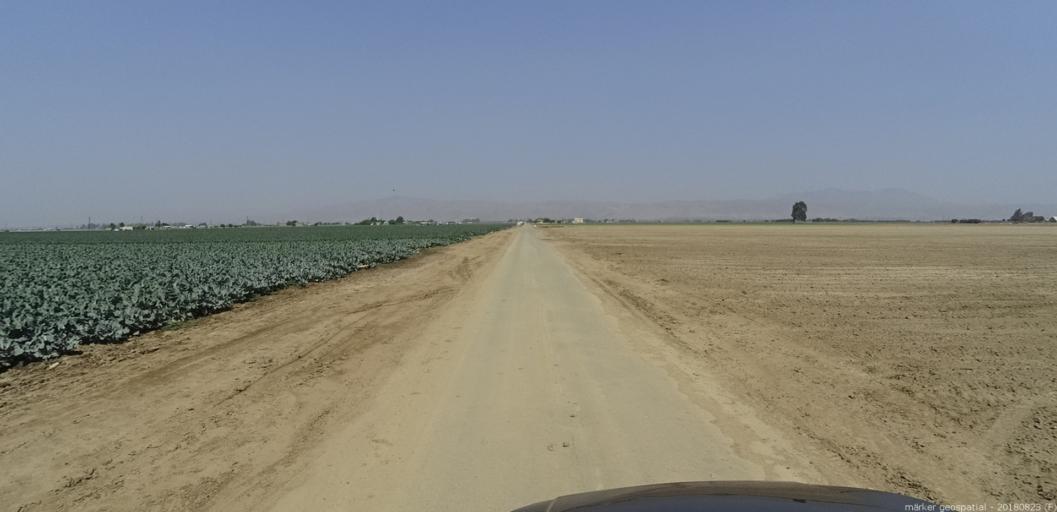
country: US
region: California
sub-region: Monterey County
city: Soledad
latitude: 36.3855
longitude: -121.3522
